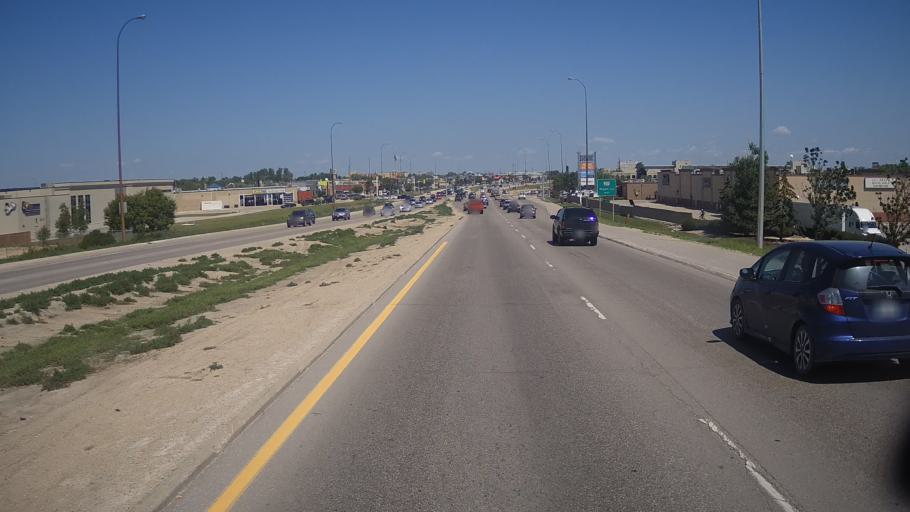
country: CA
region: Manitoba
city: Winnipeg
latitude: 49.8956
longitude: -97.0702
